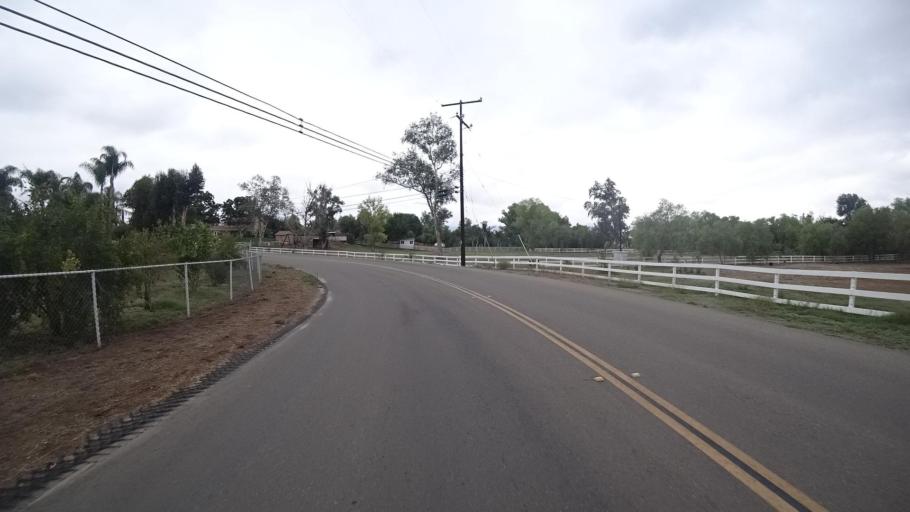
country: US
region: California
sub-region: San Diego County
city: Ramona
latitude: 33.0250
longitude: -116.8859
